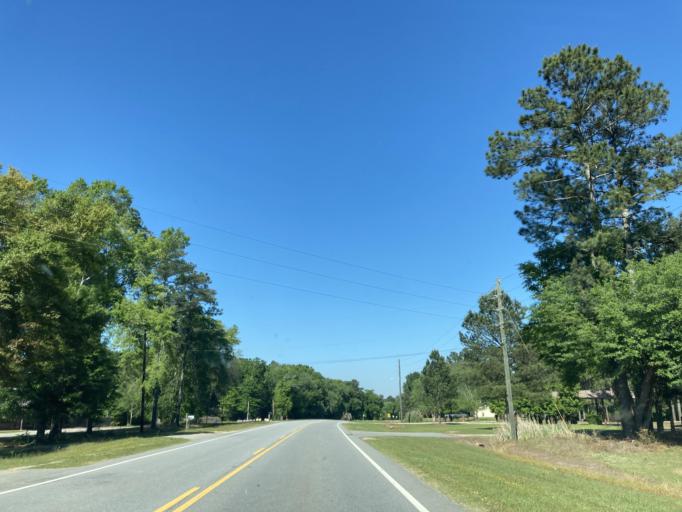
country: US
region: Georgia
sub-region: Baker County
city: Newton
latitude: 31.3265
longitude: -84.3384
